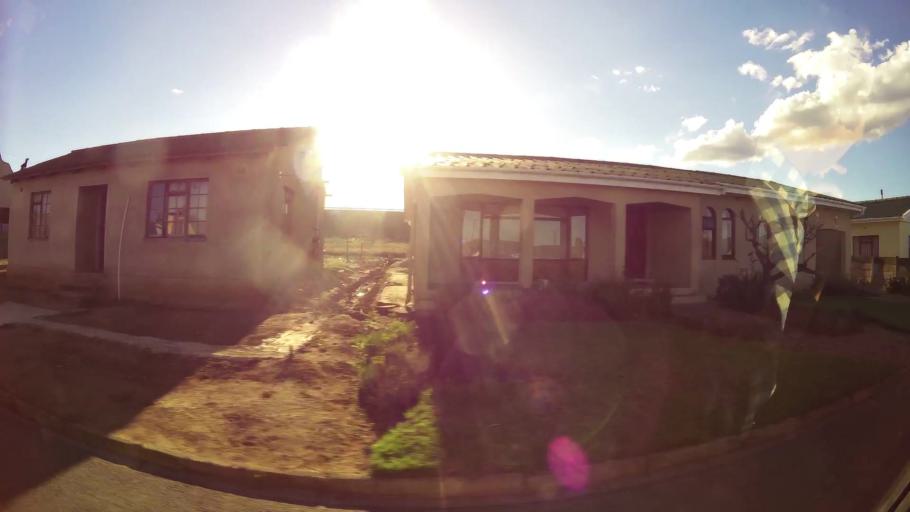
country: ZA
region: Western Cape
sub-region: Eden District Municipality
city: Riversdale
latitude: -34.1036
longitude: 20.9602
